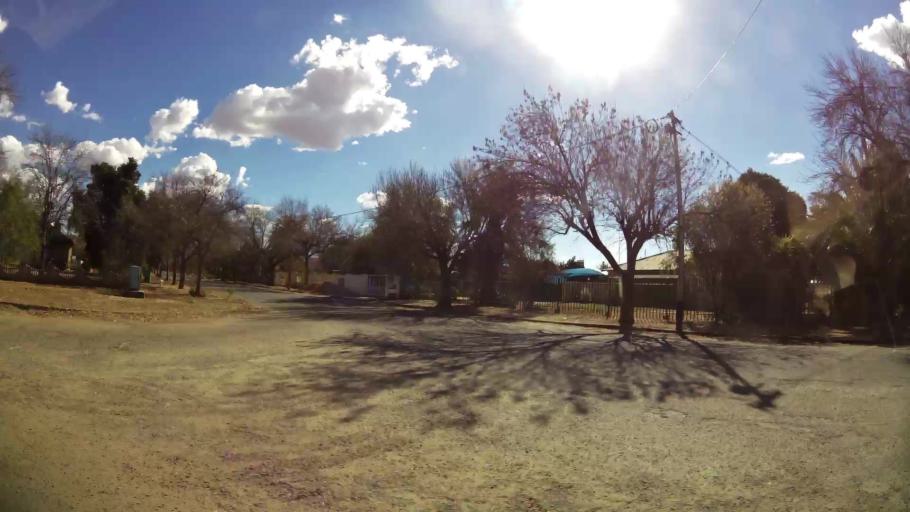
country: ZA
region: North-West
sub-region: Dr Kenneth Kaunda District Municipality
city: Klerksdorp
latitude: -26.8635
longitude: 26.6356
